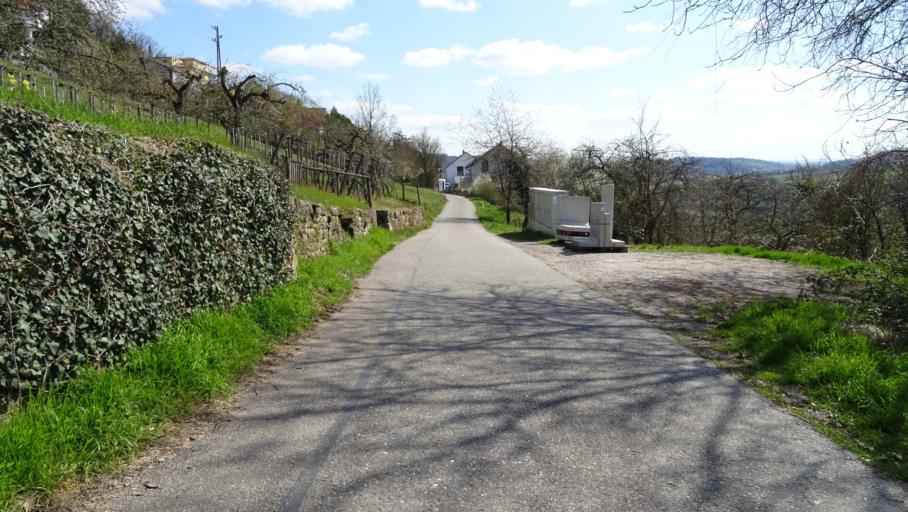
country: DE
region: Baden-Wuerttemberg
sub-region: Karlsruhe Region
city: Neckarzimmern
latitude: 49.3242
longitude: 9.1239
